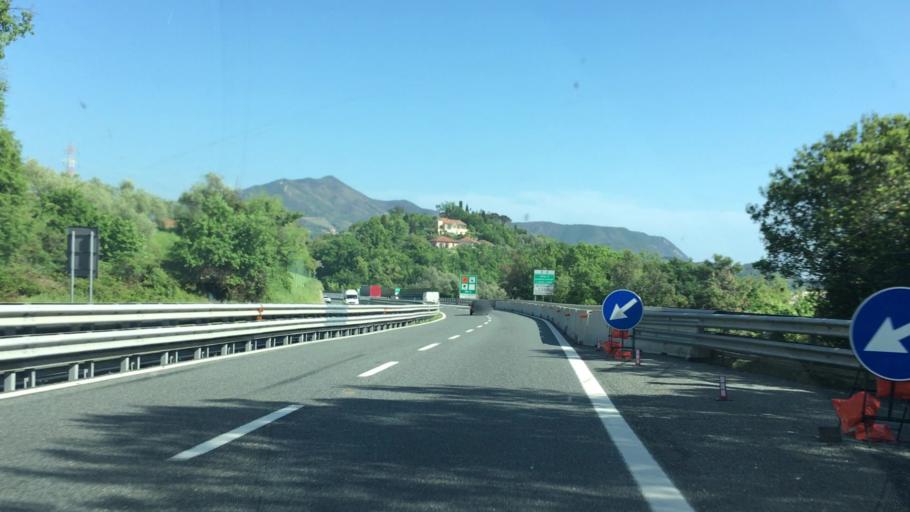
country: IT
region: Liguria
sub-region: Provincia di Genova
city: Sestri Levante
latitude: 44.2818
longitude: 9.4103
